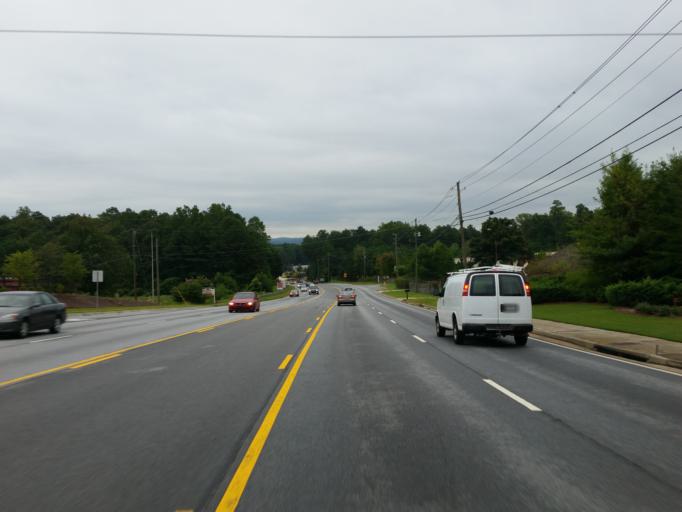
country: US
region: Georgia
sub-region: Cobb County
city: Mableton
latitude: 33.8102
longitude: -84.5347
